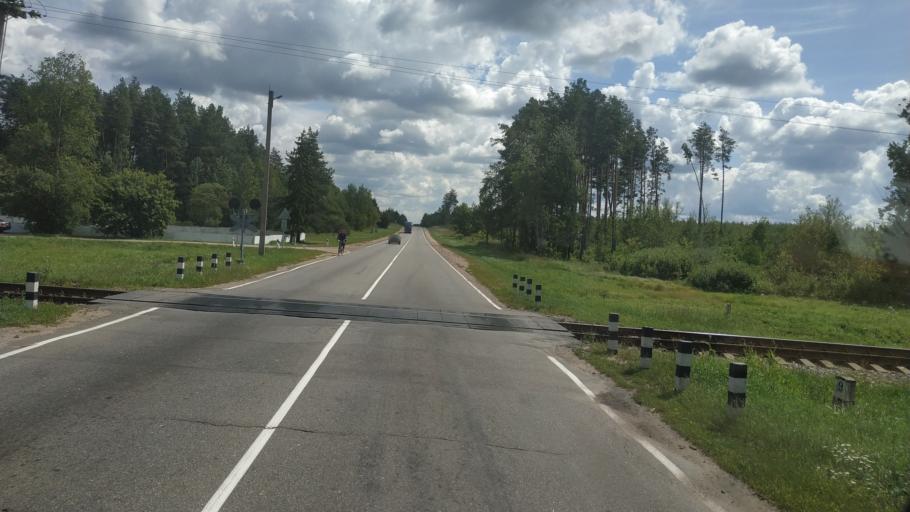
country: BY
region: Mogilev
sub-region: Mahilyowski Rayon
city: Veyno
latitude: 53.8287
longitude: 30.4133
